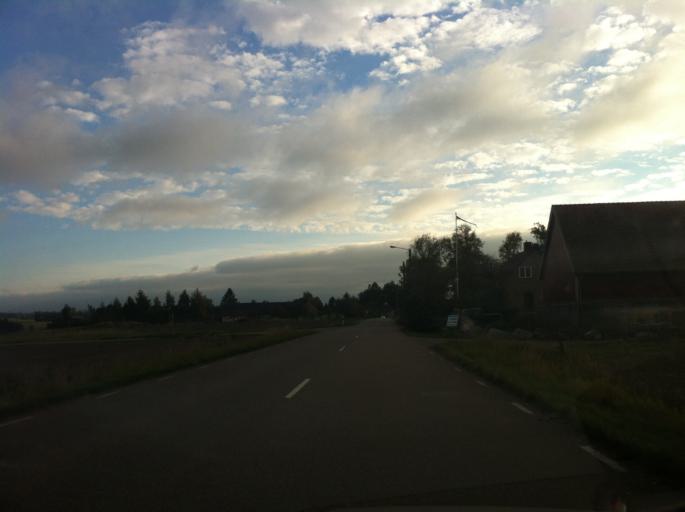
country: SE
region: Skane
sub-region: Helsingborg
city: Barslov
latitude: 56.0085
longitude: 12.8217
